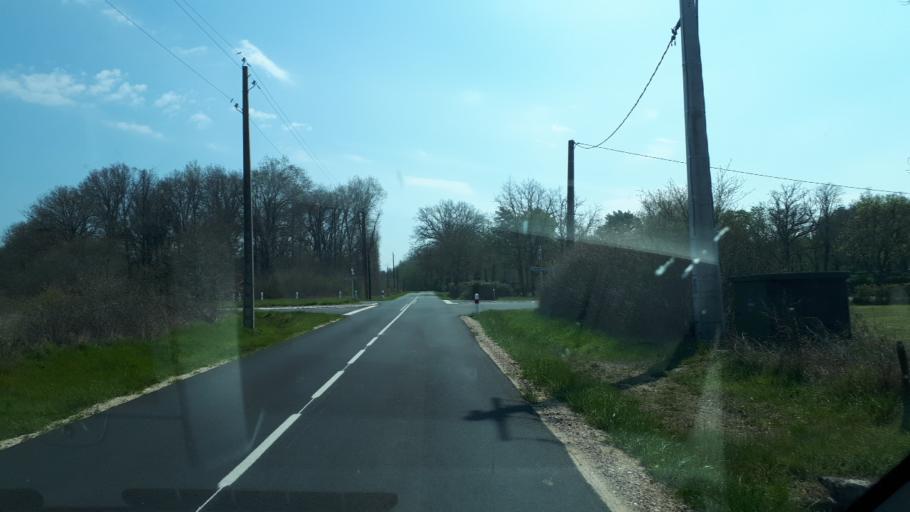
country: FR
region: Centre
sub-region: Departement du Loir-et-Cher
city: Selles-Saint-Denis
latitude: 47.3434
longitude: 1.8936
